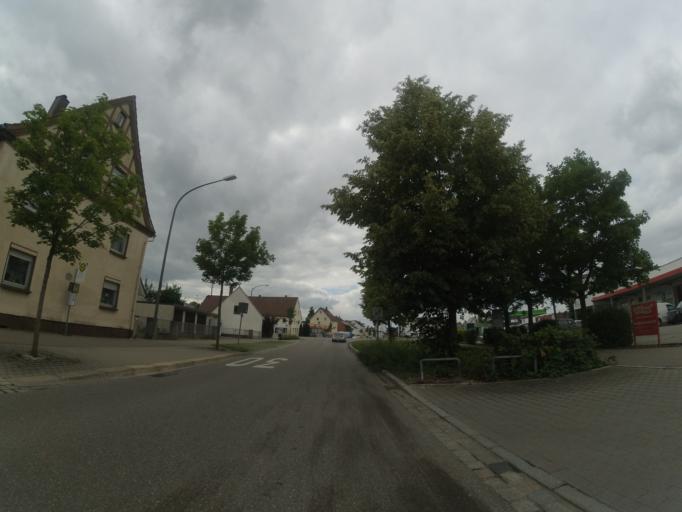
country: DE
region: Bavaria
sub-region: Swabia
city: Neu-Ulm
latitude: 48.4020
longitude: 10.0225
